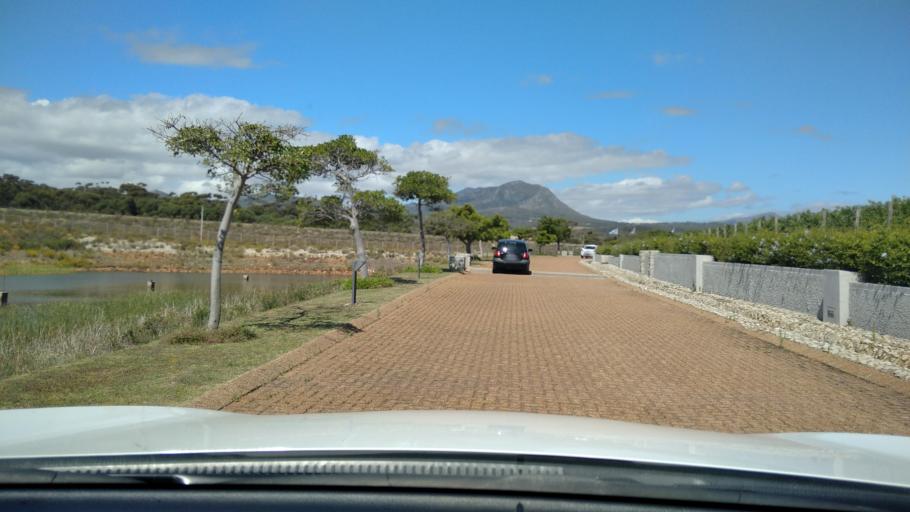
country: ZA
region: Western Cape
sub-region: Overberg District Municipality
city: Hermanus
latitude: -34.3456
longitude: 19.1360
